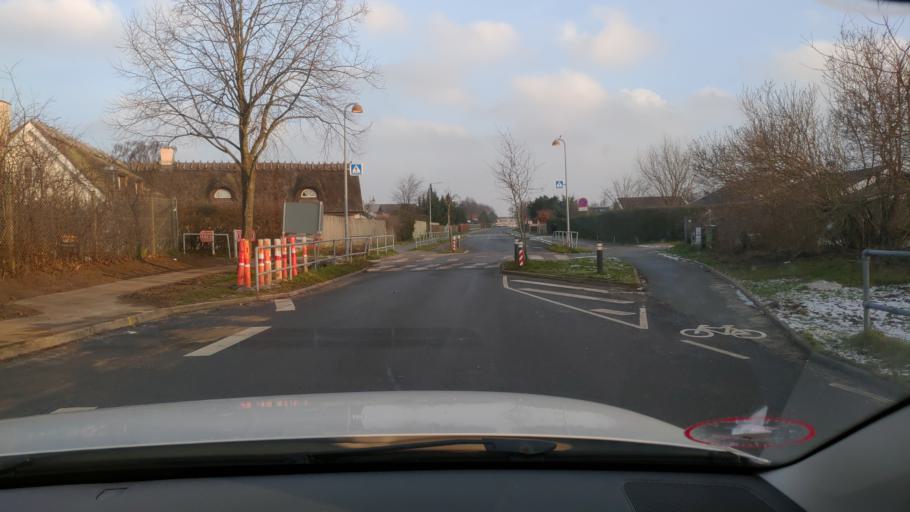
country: DK
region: Zealand
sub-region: Solrod Kommune
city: Solrod Strand
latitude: 55.5405
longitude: 12.2208
